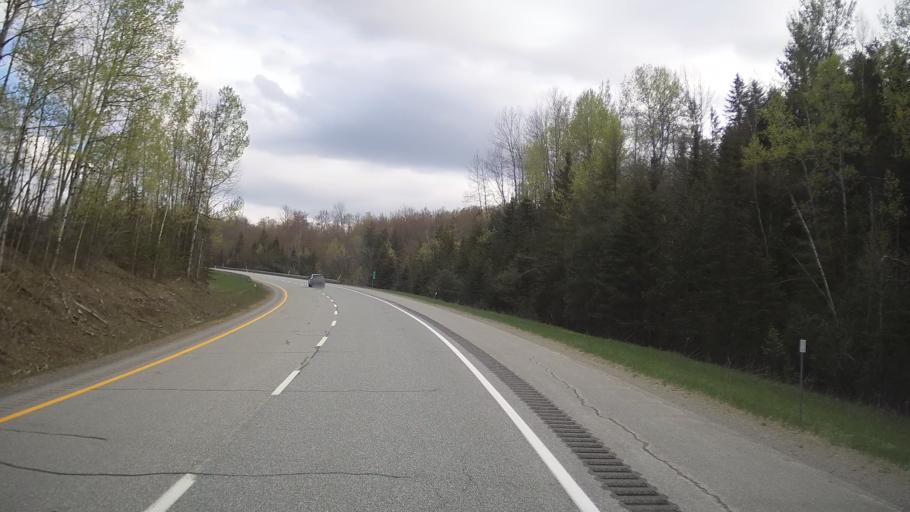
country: CA
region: Quebec
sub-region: Estrie
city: Magog
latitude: 45.1755
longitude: -72.0748
